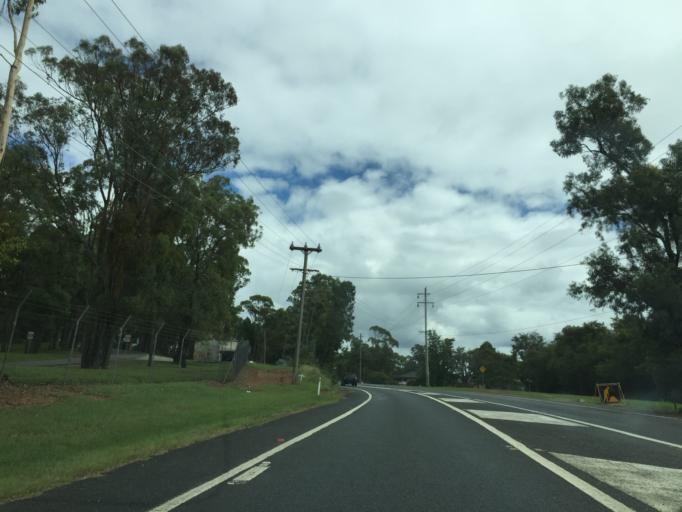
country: AU
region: New South Wales
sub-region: Hawkesbury
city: Richmond
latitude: -33.5729
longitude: 150.7123
